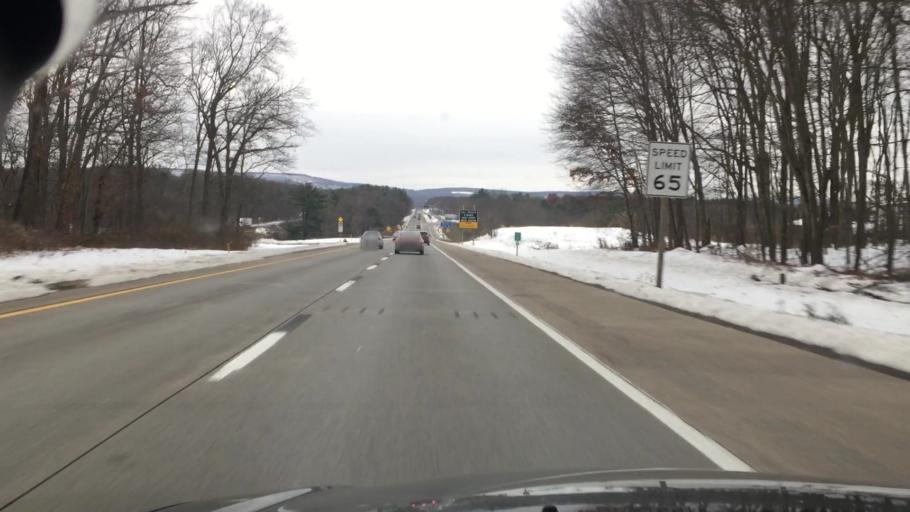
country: US
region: Pennsylvania
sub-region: Luzerne County
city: Nanticoke
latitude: 41.1379
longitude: -75.9635
